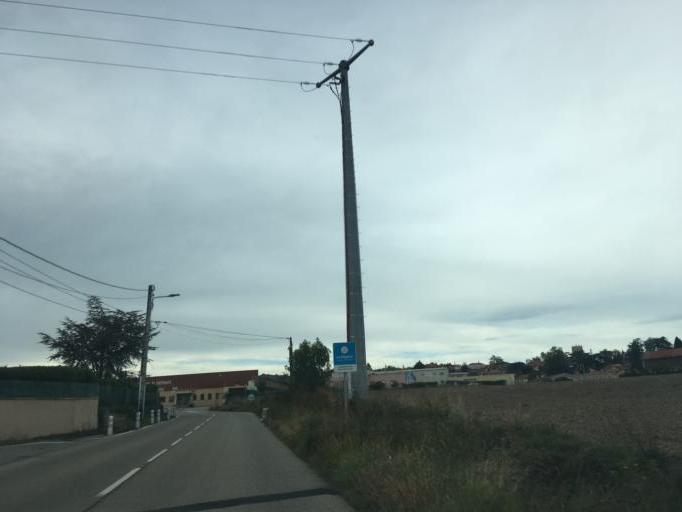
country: FR
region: Rhone-Alpes
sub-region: Departement de la Loire
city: Saint-Martin-la-Plaine
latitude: 45.5393
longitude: 4.5941
